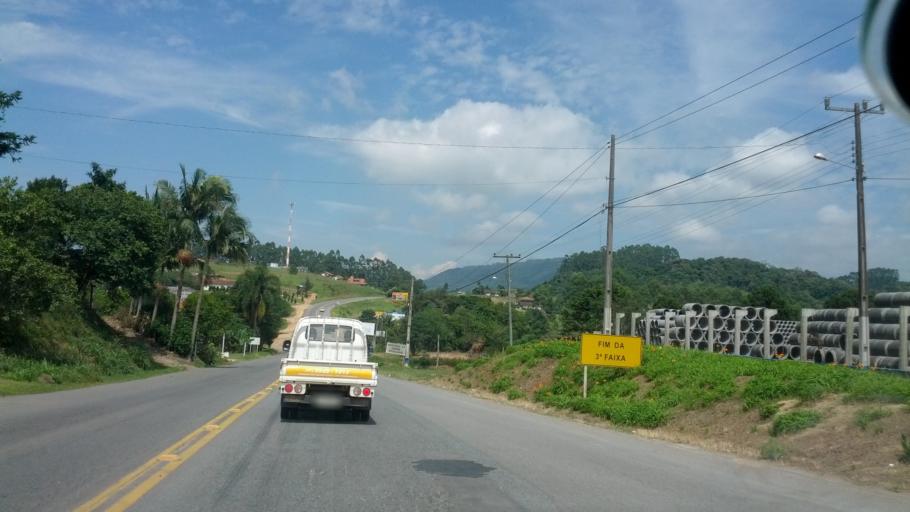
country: BR
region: Santa Catarina
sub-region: Ibirama
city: Ibirama
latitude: -27.1082
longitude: -49.5243
